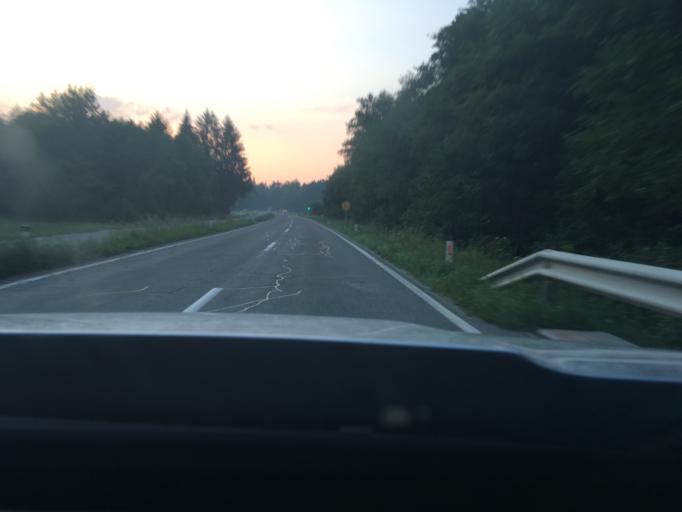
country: SI
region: Kocevje
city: Kocevje
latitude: 45.6775
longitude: 14.8259
